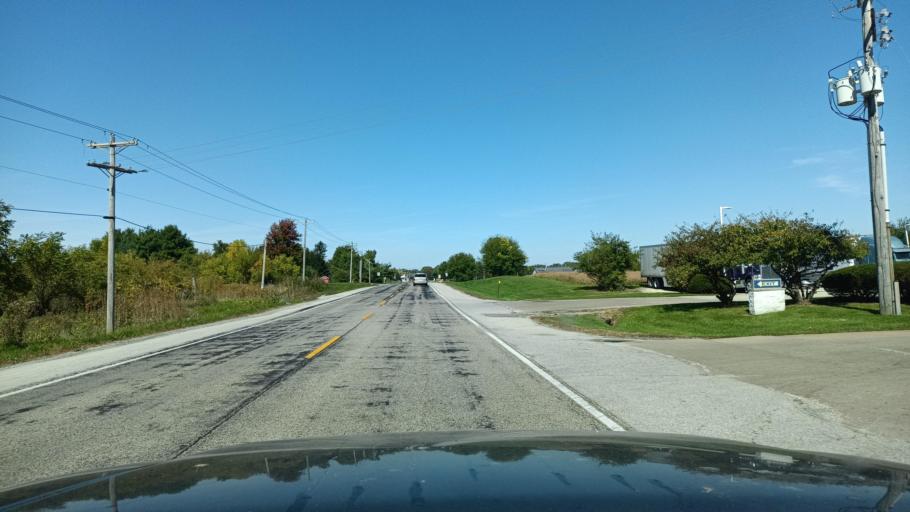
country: US
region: Illinois
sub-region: Champaign County
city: Lake of the Woods
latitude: 40.1917
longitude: -88.3653
